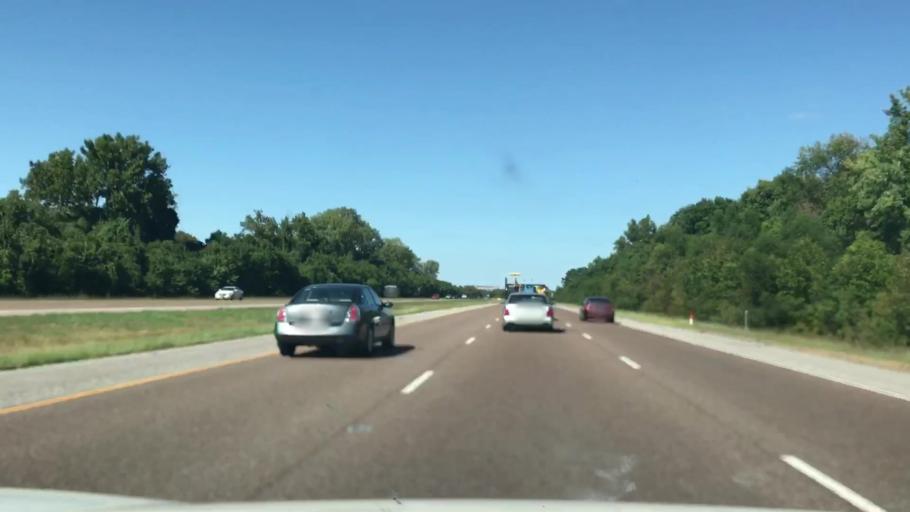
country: US
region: Illinois
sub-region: Madison County
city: Collinsville
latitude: 38.7056
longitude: -90.0287
